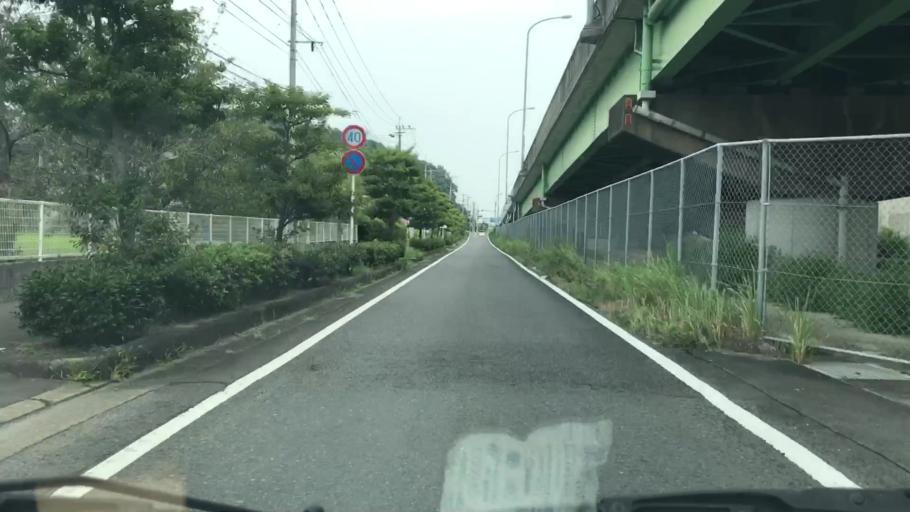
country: JP
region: Saga Prefecture
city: Saga-shi
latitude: 33.2233
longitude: 130.1734
